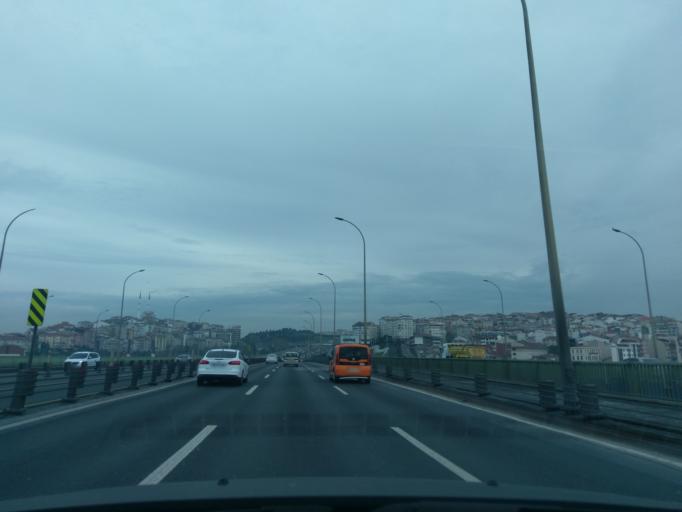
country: TR
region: Istanbul
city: Istanbul
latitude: 41.0438
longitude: 28.9421
